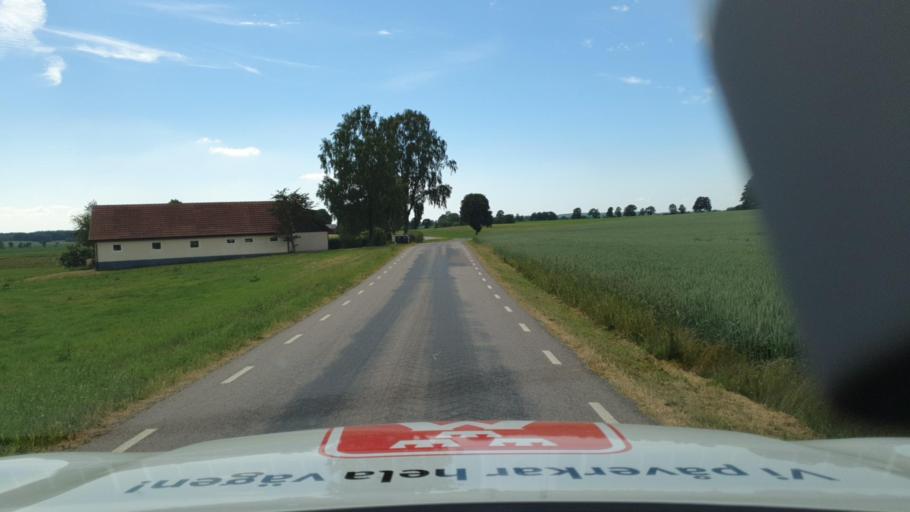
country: SE
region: Skane
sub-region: Tomelilla Kommun
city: Tomelilla
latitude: 55.6274
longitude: 13.8520
